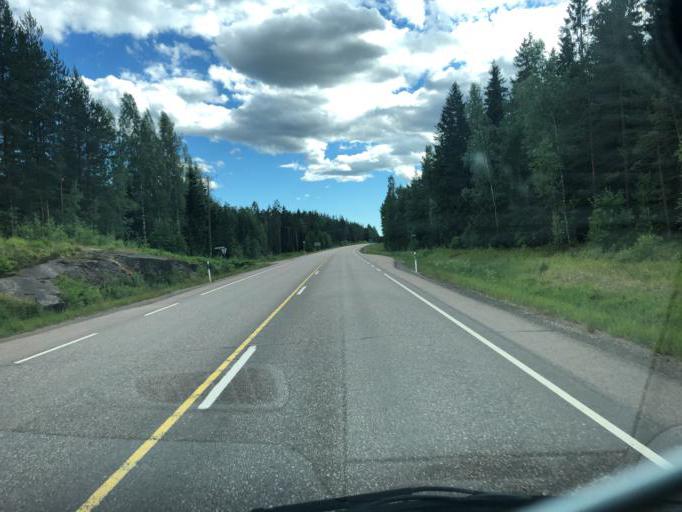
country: FI
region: Southern Savonia
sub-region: Mikkeli
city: Maentyharju
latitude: 61.0727
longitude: 27.0585
